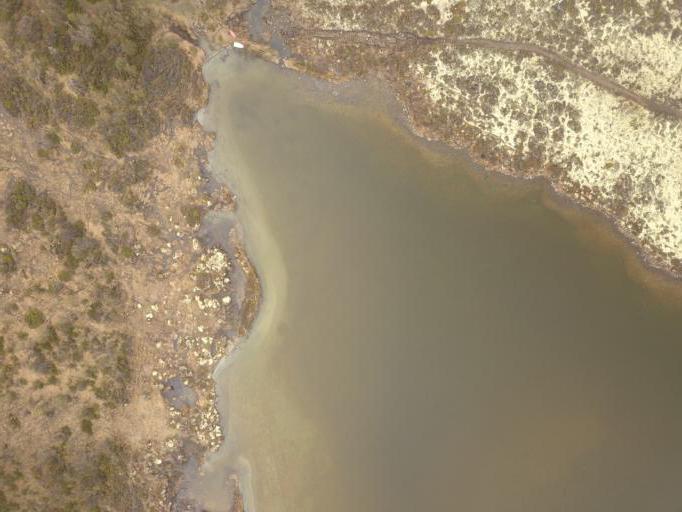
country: NO
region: Hedmark
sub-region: Folldal
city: Folldal
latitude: 62.2296
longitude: 9.6462
